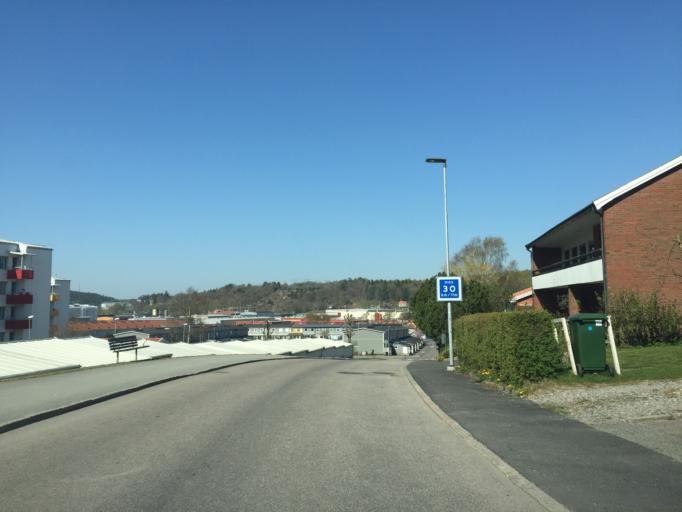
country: SE
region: Vaestra Goetaland
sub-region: Kungalvs Kommun
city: Kungalv
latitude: 57.8765
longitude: 11.9894
